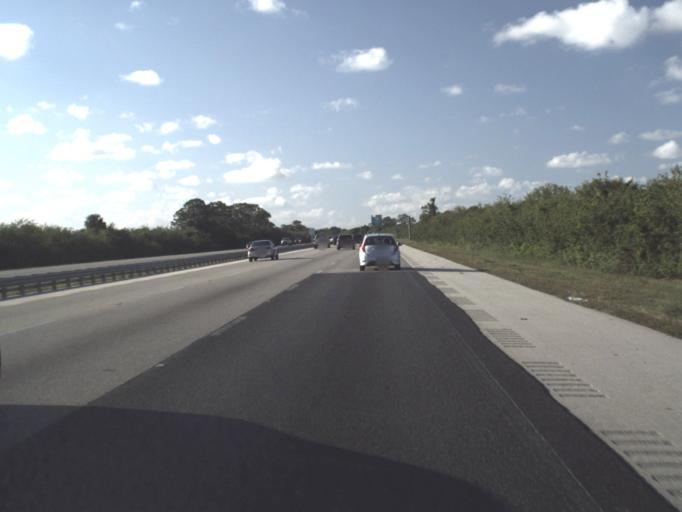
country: US
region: Florida
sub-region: Brevard County
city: Rockledge
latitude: 28.2766
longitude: -80.7318
